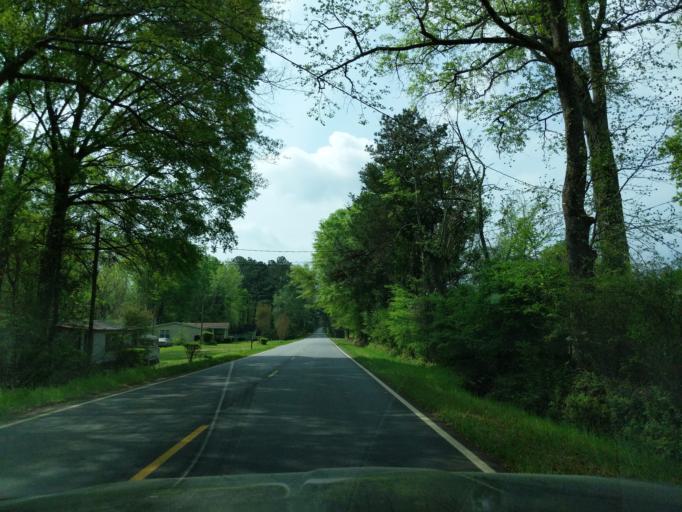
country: US
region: Georgia
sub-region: Columbia County
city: Appling
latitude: 33.6544
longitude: -82.3372
